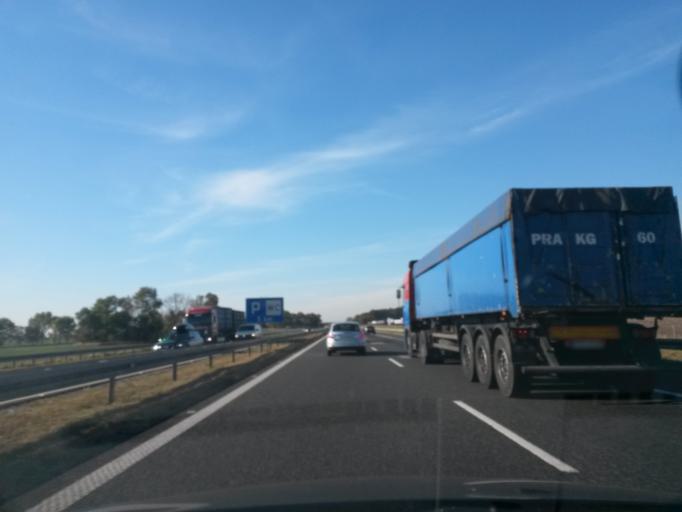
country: PL
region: Lower Silesian Voivodeship
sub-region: Powiat wroclawski
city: Zorawina
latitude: 50.9960
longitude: 17.0458
